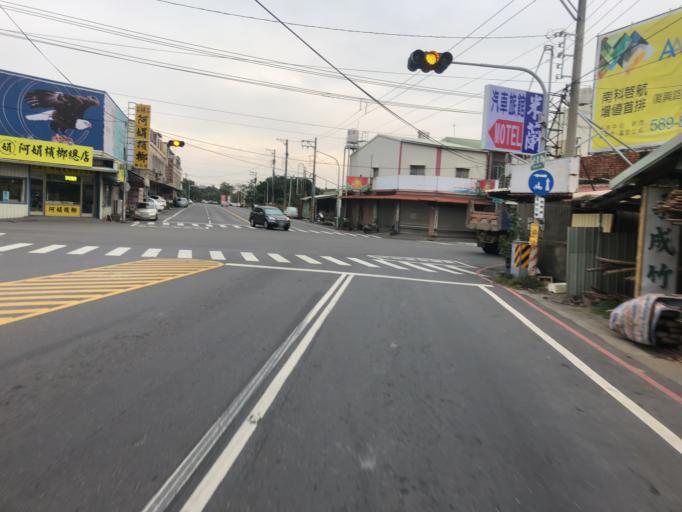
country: TW
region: Taiwan
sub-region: Tainan
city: Tainan
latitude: 23.1336
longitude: 120.2848
